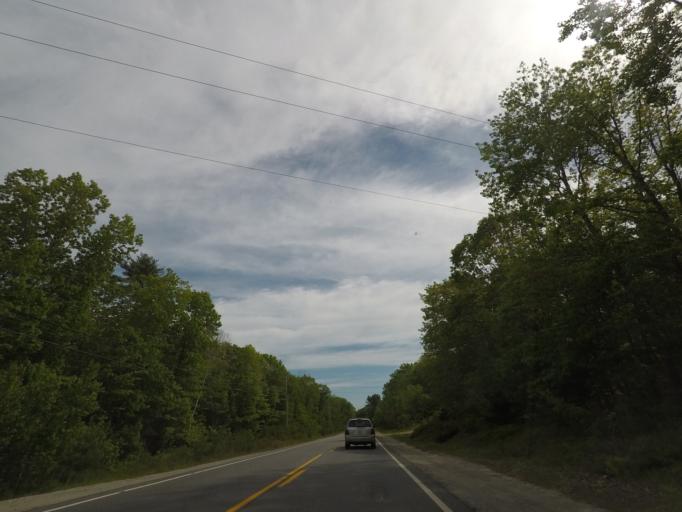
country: US
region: Maine
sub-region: Sagadahoc County
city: Richmond
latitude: 44.1073
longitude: -69.7827
